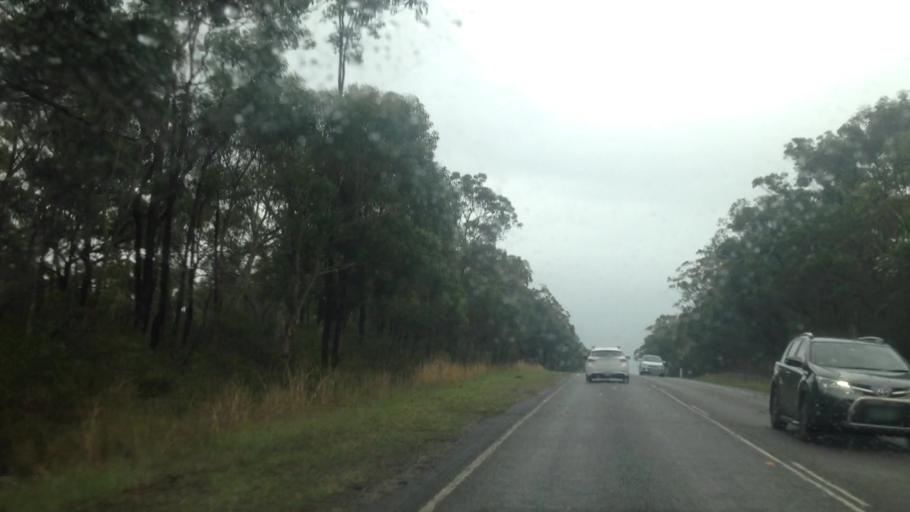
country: AU
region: New South Wales
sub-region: Lake Macquarie Shire
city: Dora Creek
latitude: -33.1446
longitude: 151.4785
